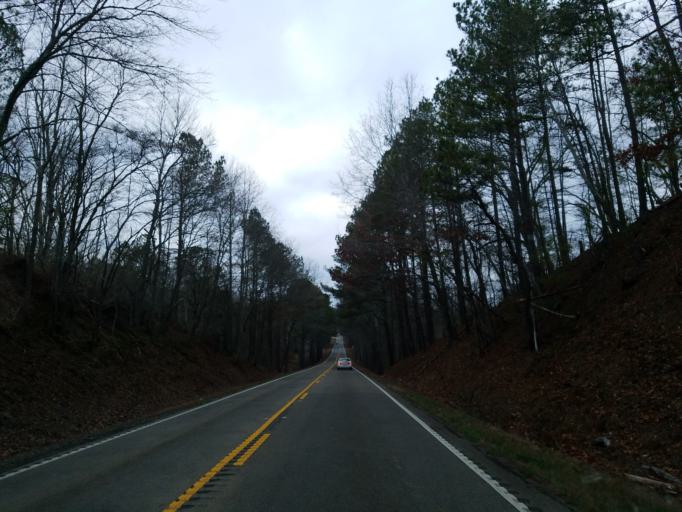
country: US
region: Georgia
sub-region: Cherokee County
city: Canton
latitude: 34.3368
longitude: -84.5680
